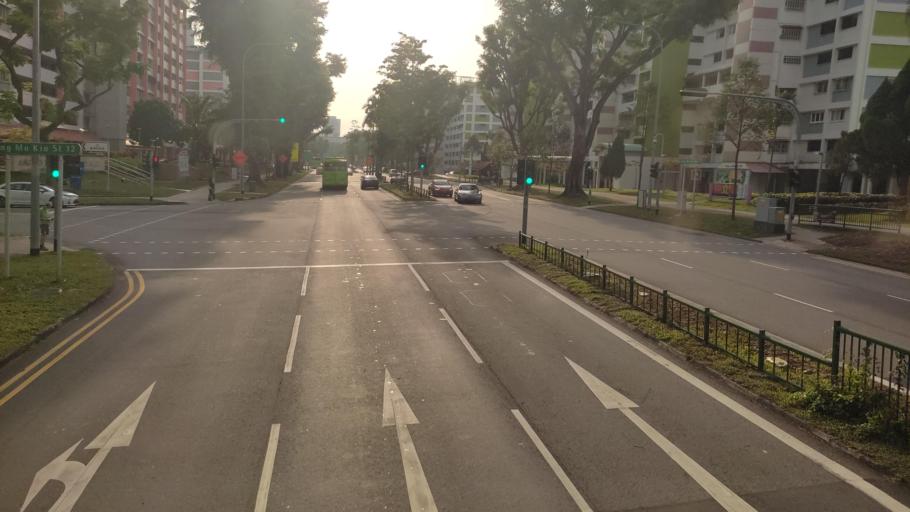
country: SG
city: Singapore
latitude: 1.3695
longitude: 103.8424
